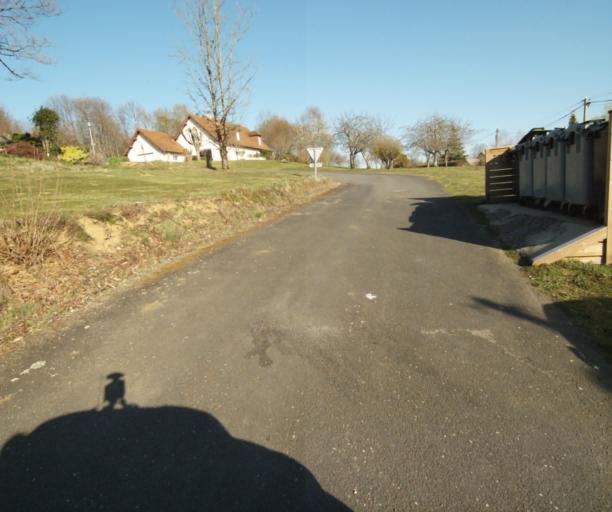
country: FR
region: Limousin
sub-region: Departement de la Correze
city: Saint-Clement
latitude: 45.3412
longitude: 1.6744
